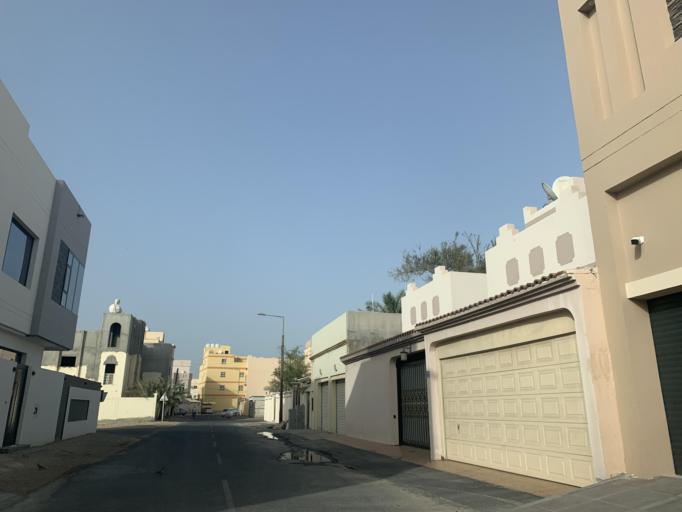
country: BH
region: Central Governorate
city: Madinat Hamad
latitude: 26.1568
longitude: 50.5094
